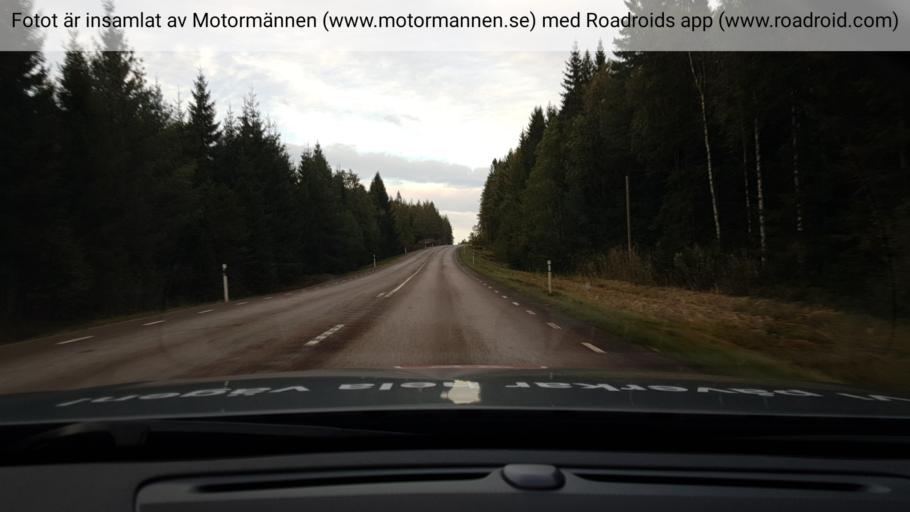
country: SE
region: Vaestra Goetaland
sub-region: Amals Kommun
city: Amal
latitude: 59.0676
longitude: 12.5539
